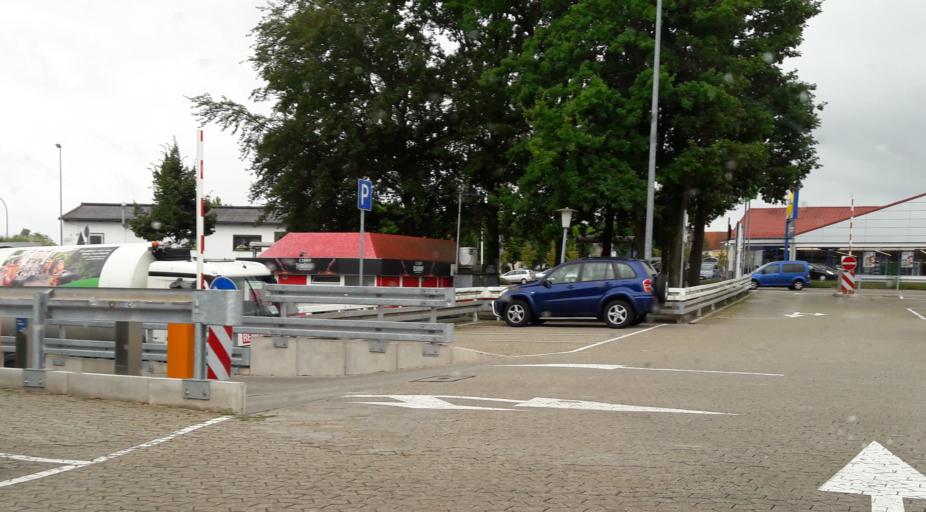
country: DE
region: Saarland
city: Spiesen-Elversberg
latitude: 49.3178
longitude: 7.1233
